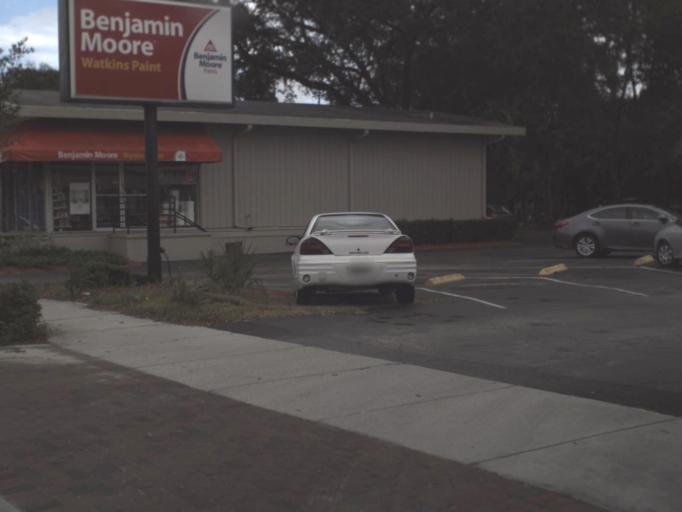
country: US
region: Florida
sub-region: Orange County
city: Winter Park
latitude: 28.5917
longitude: -81.3581
